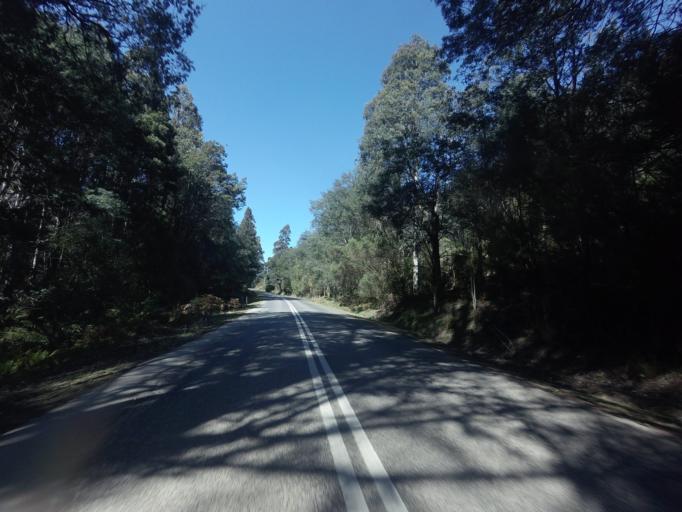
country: AU
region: Tasmania
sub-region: Derwent Valley
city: New Norfolk
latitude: -42.7612
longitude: 146.6080
